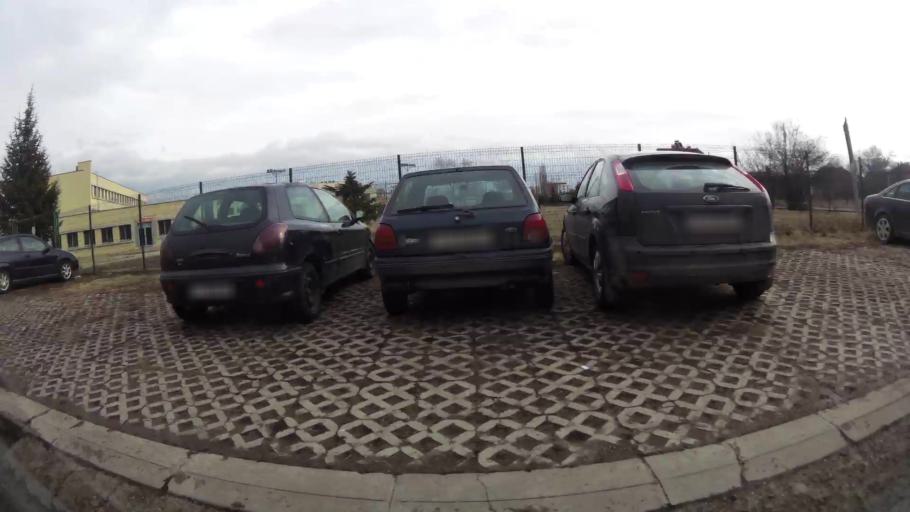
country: BG
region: Sofia-Capital
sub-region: Stolichna Obshtina
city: Sofia
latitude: 42.7453
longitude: 23.2725
